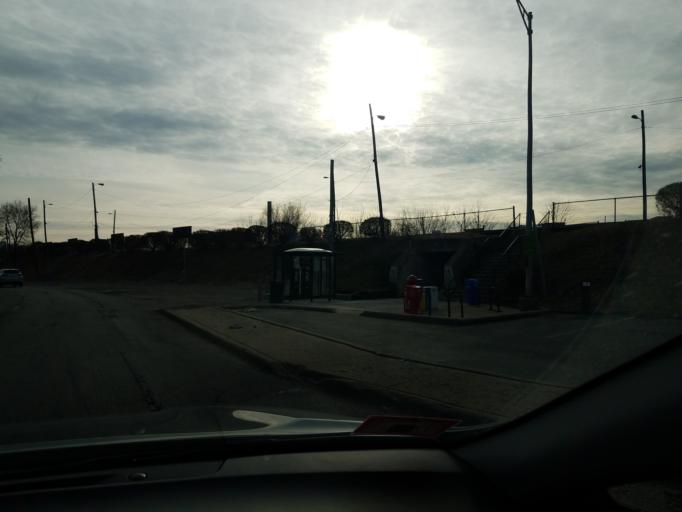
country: US
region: Illinois
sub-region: Cook County
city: Lincolnwood
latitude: 41.9788
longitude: -87.7554
